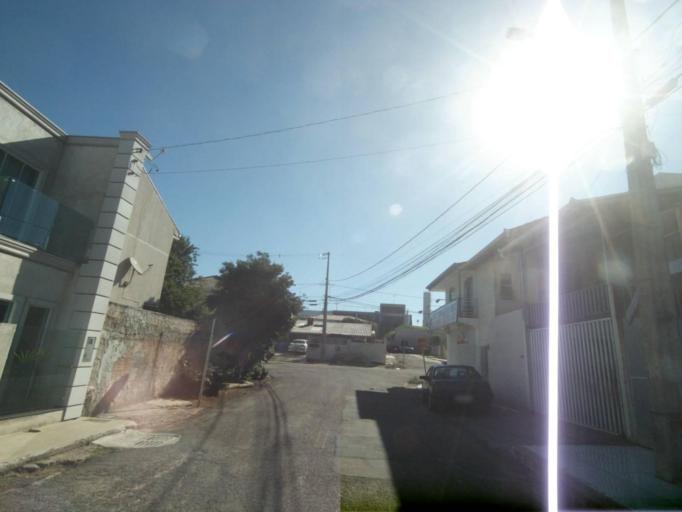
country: BR
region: Parana
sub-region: Curitiba
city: Curitiba
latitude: -25.4632
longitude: -49.3537
